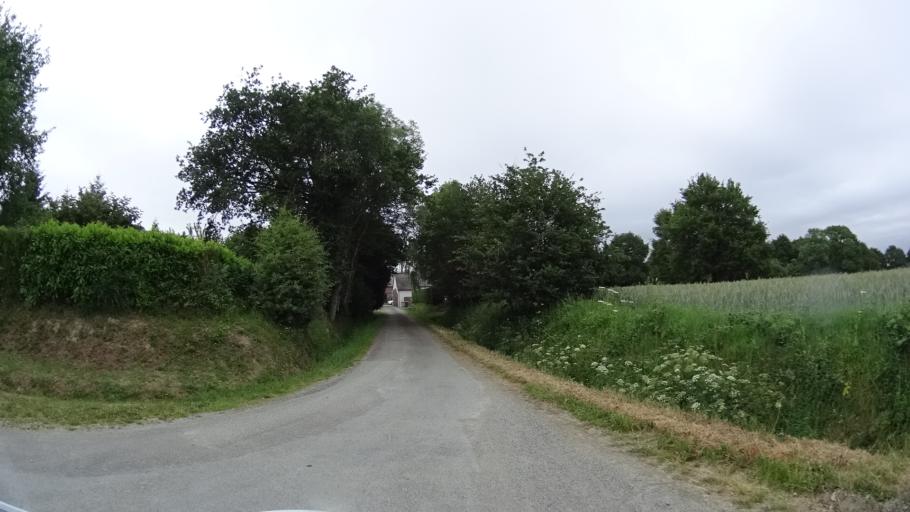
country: FR
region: Brittany
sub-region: Departement d'Ille-et-Vilaine
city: Crevin
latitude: 47.9610
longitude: -1.6785
